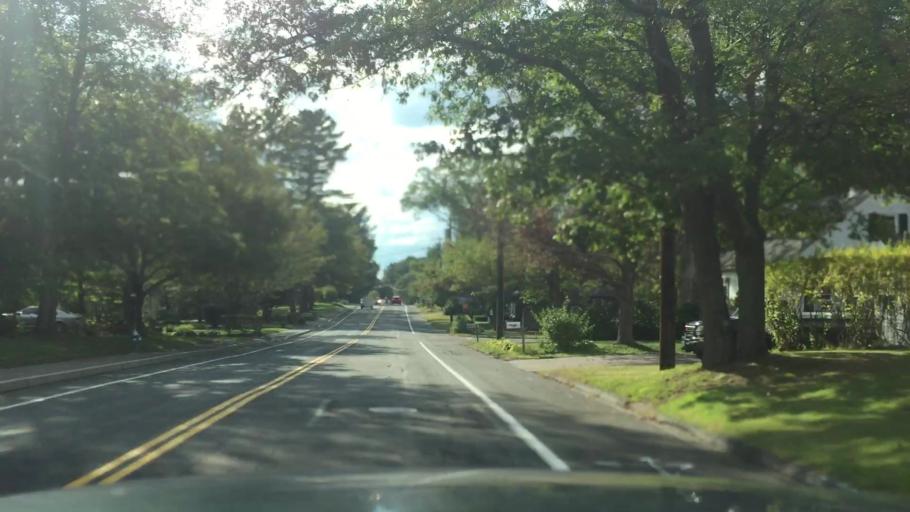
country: US
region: Massachusetts
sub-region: Norfolk County
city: Medway
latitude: 42.1571
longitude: -71.4170
